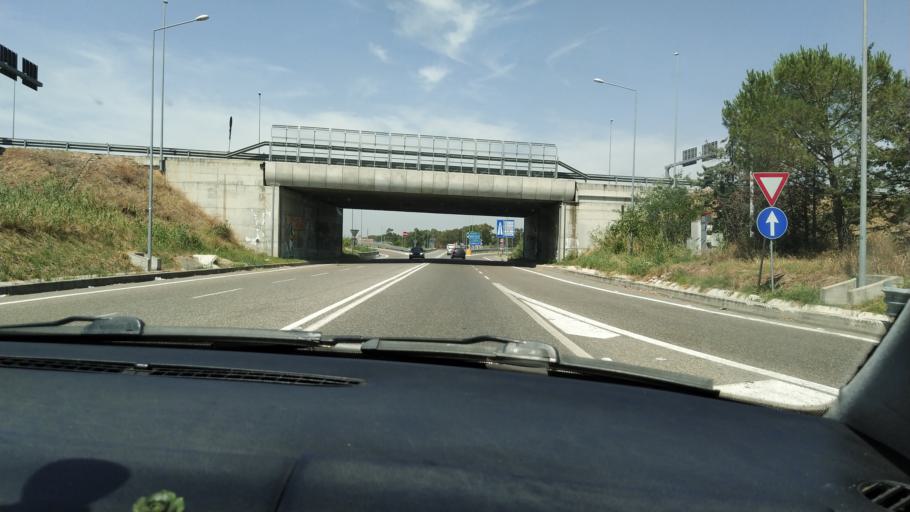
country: IT
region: Apulia
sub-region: Provincia di Taranto
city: Marina di Ginosa
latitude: 40.3774
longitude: 16.7907
